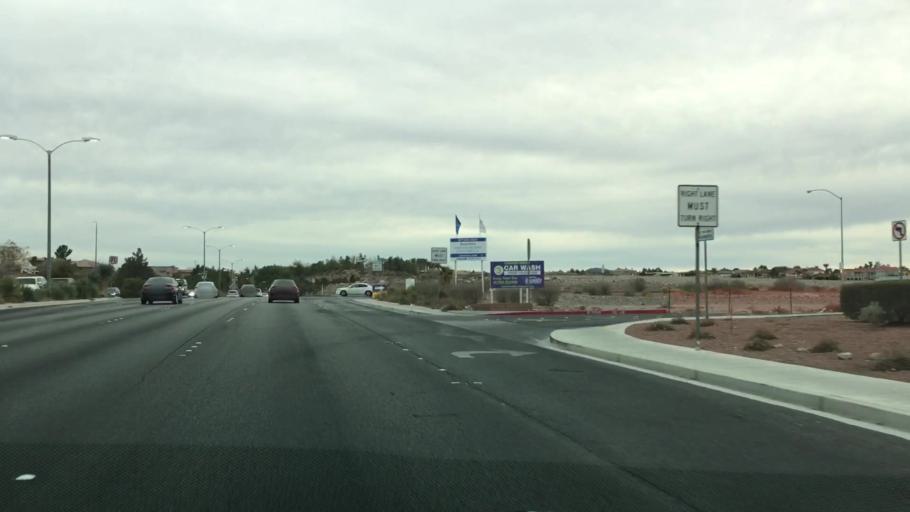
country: US
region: Nevada
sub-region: Clark County
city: Whitney
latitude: 35.9864
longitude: -115.0868
